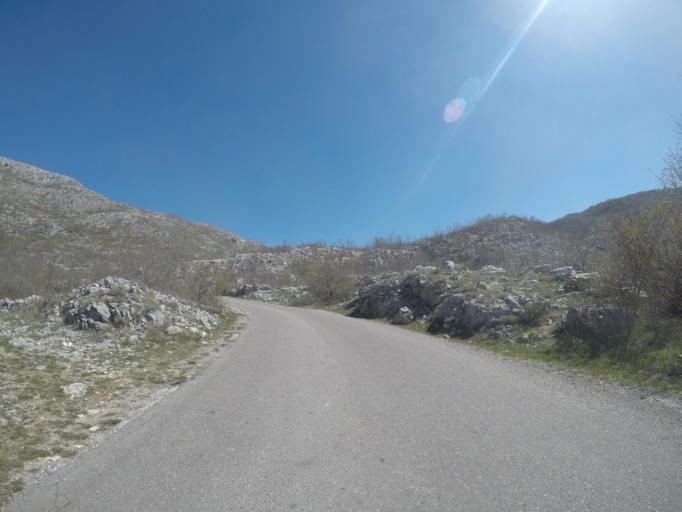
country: ME
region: Cetinje
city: Cetinje
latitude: 42.4972
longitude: 18.8787
